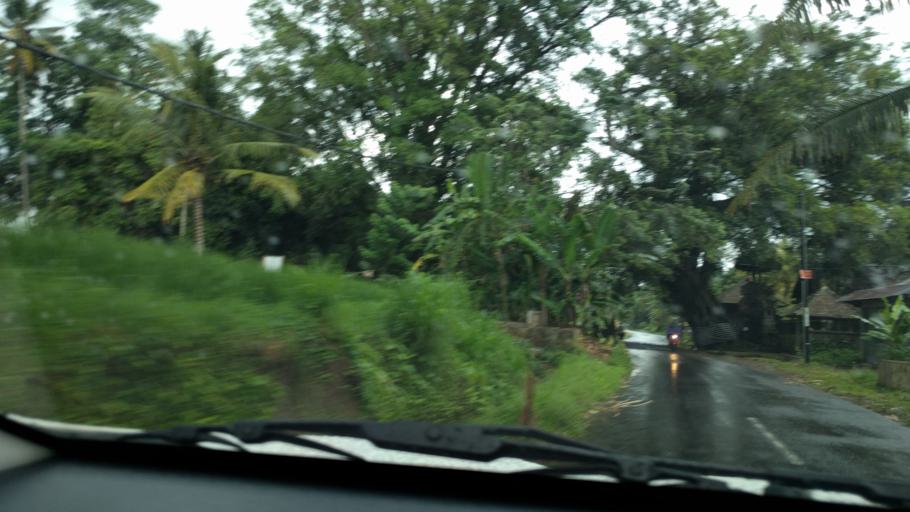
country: ID
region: Bali
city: Bunutan
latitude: -8.4787
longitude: 115.2588
